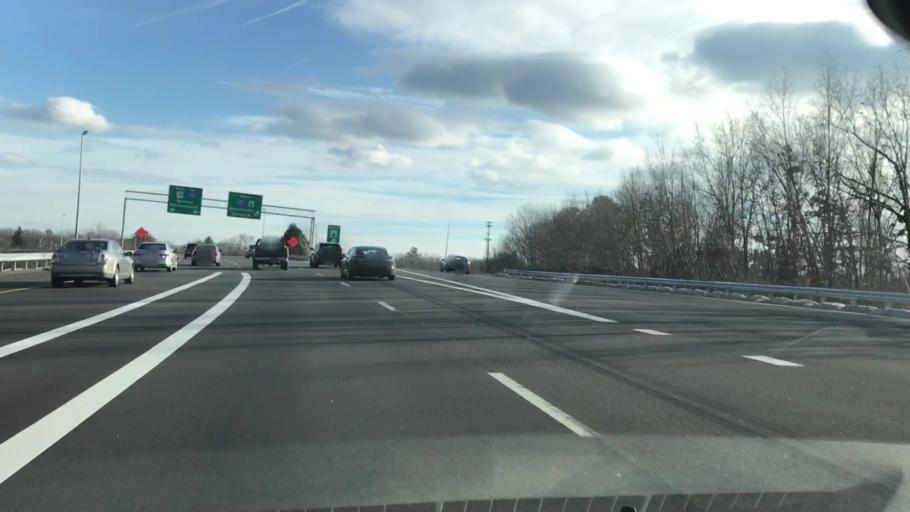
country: US
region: New Hampshire
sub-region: Hillsborough County
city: Bedford
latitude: 42.9486
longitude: -71.4740
